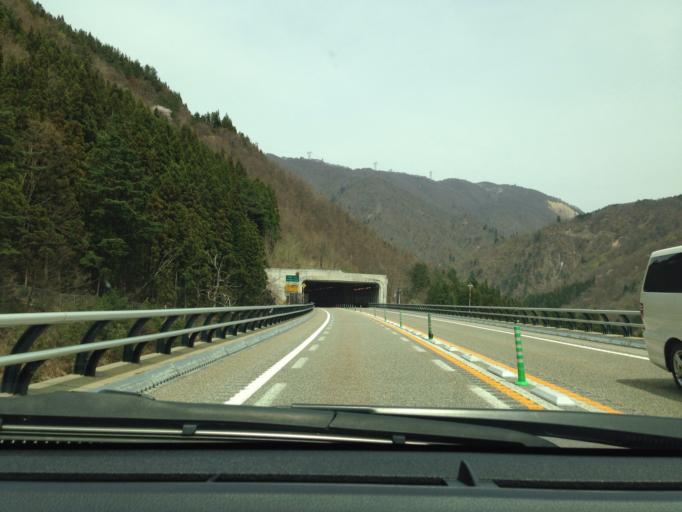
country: JP
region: Toyama
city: Fukumitsu
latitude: 36.2820
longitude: 136.9008
